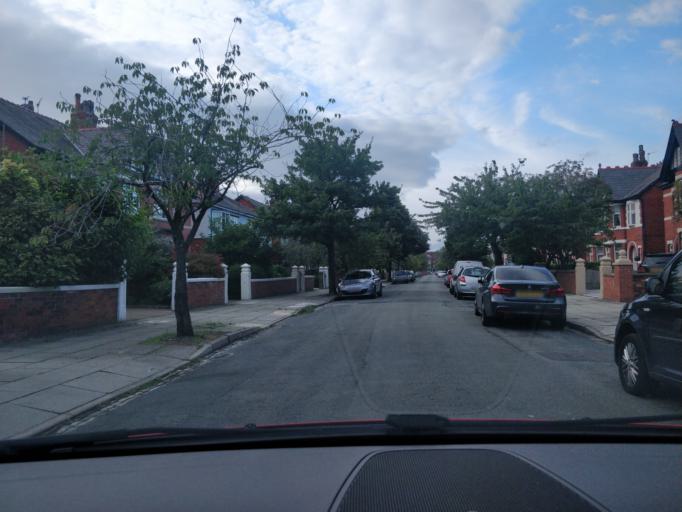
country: GB
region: England
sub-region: Sefton
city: Southport
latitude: 53.6484
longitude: -2.9827
